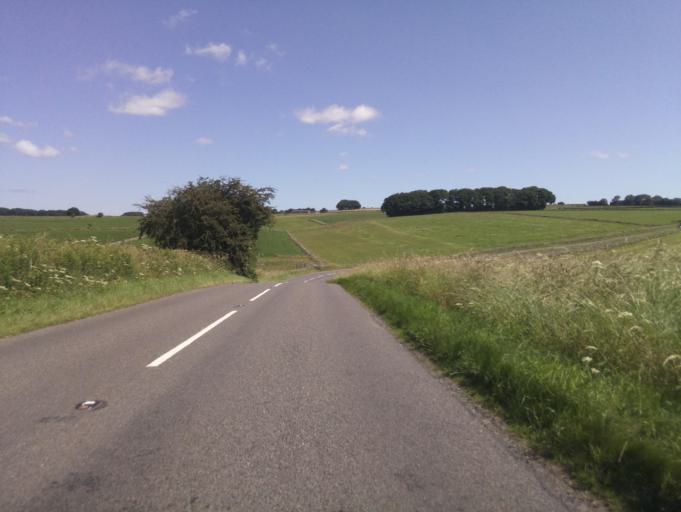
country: GB
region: England
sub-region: Derbyshire
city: Tideswell
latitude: 53.1974
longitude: -1.7587
